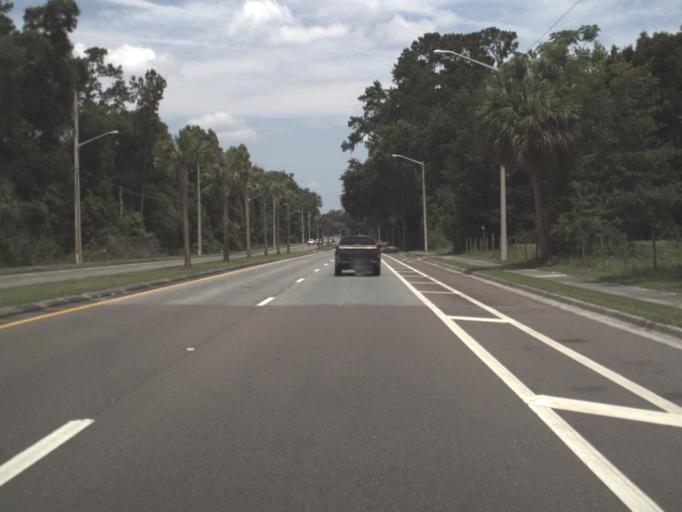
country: US
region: Florida
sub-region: Alachua County
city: Gainesville
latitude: 29.6282
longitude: -82.2617
